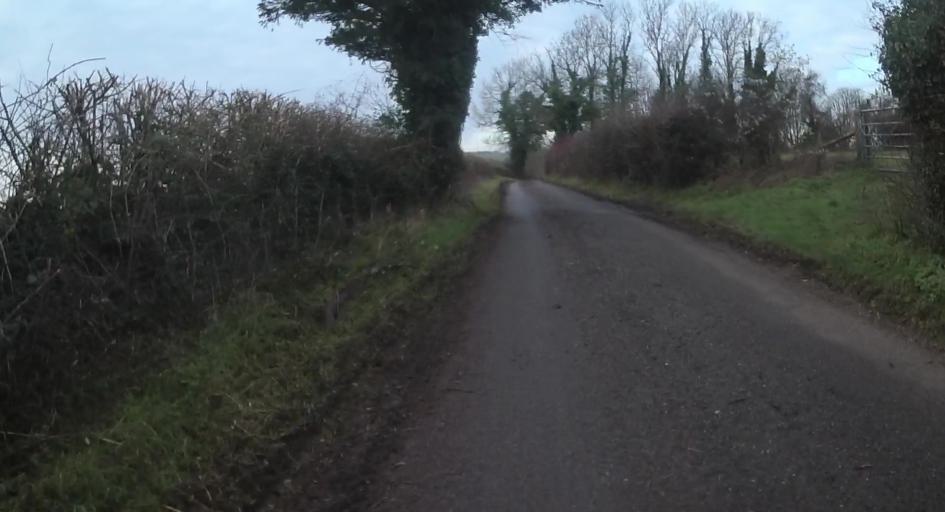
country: GB
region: England
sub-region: Hampshire
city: Kingsclere
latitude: 51.2873
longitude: -1.1923
